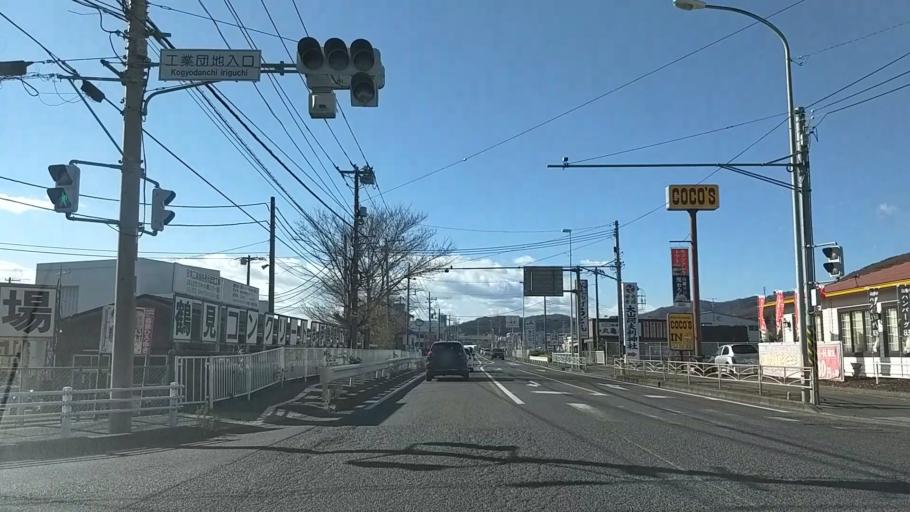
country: JP
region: Kanagawa
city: Isehara
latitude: 35.3962
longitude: 139.2912
